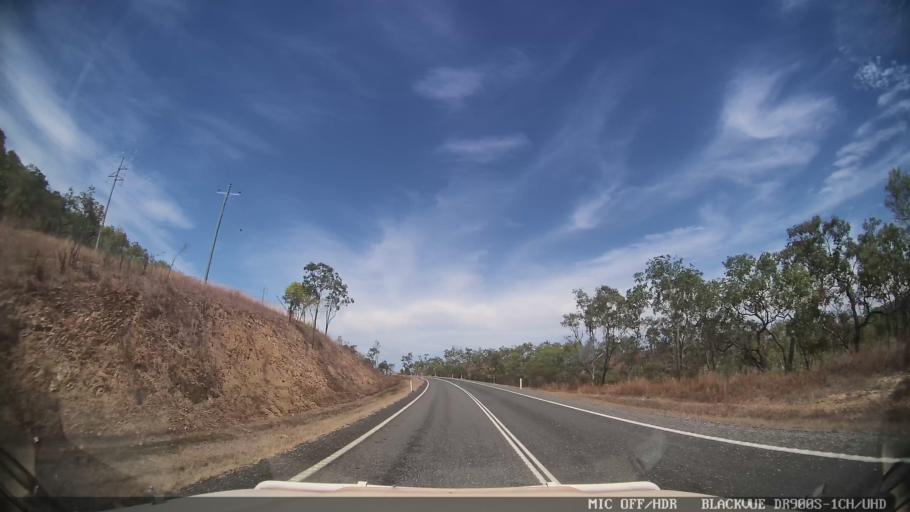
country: AU
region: Queensland
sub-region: Cook
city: Cooktown
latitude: -15.7024
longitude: 145.0258
